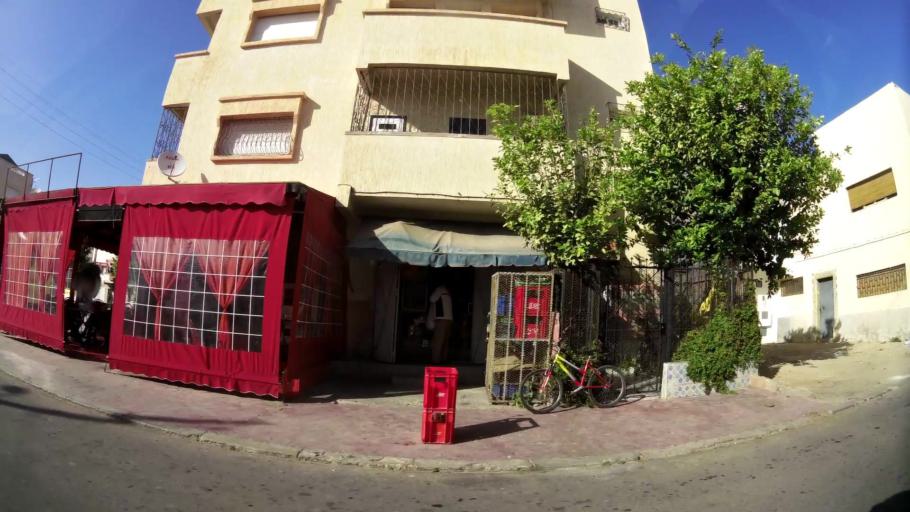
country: MA
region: Souss-Massa-Draa
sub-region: Agadir-Ida-ou-Tnan
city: Agadir
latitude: 30.4329
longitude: -9.5788
